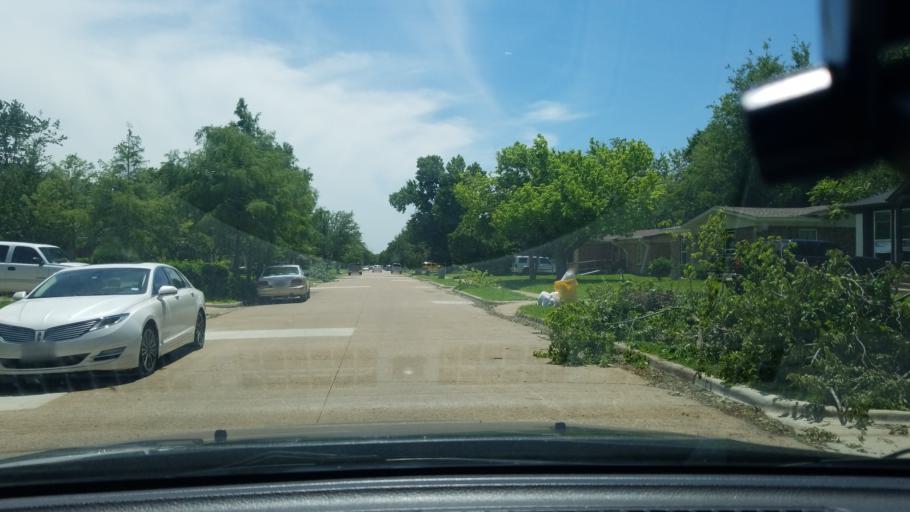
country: US
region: Texas
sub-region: Dallas County
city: Mesquite
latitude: 32.7870
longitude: -96.6126
